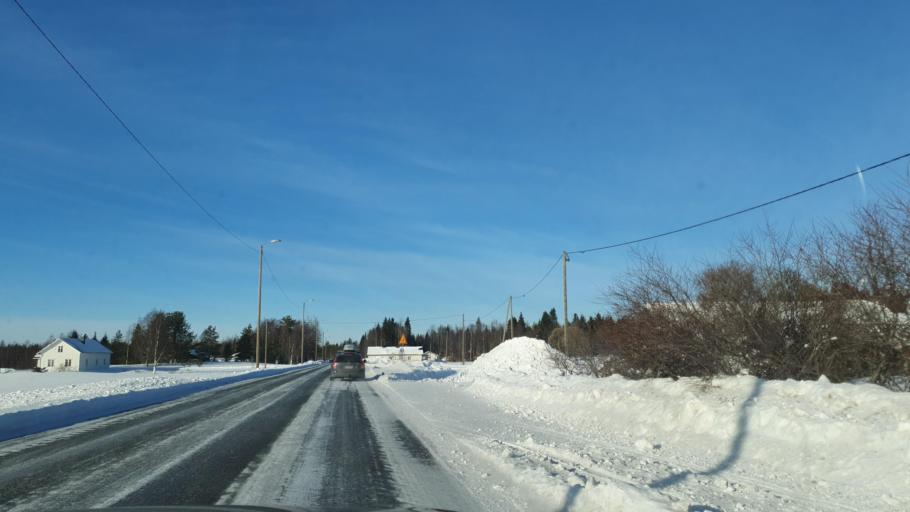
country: FI
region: Lapland
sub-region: Torniolaakso
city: Ylitornio
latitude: 66.2405
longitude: 23.7420
